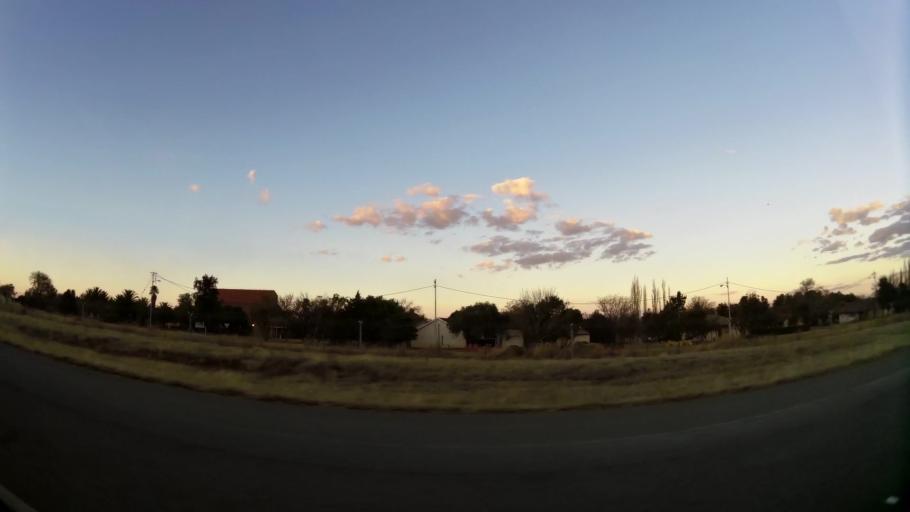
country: ZA
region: North-West
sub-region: Dr Kenneth Kaunda District Municipality
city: Potchefstroom
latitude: -26.6809
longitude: 27.0753
